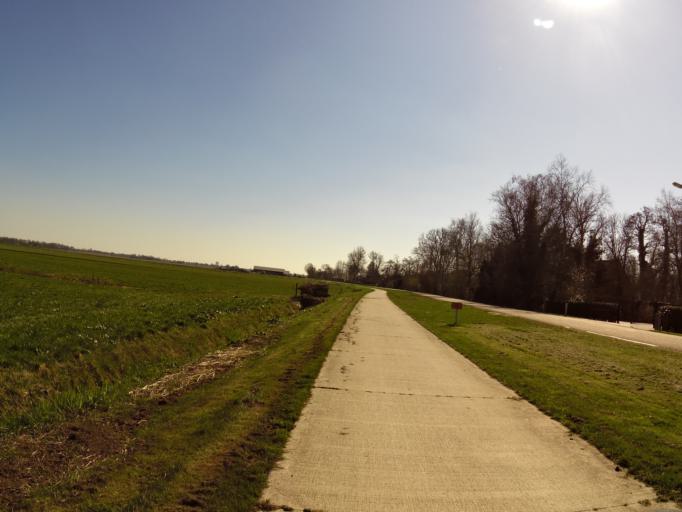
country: NL
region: Overijssel
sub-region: Gemeente Steenwijkerland
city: Blokzijl
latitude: 52.7653
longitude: 5.9921
